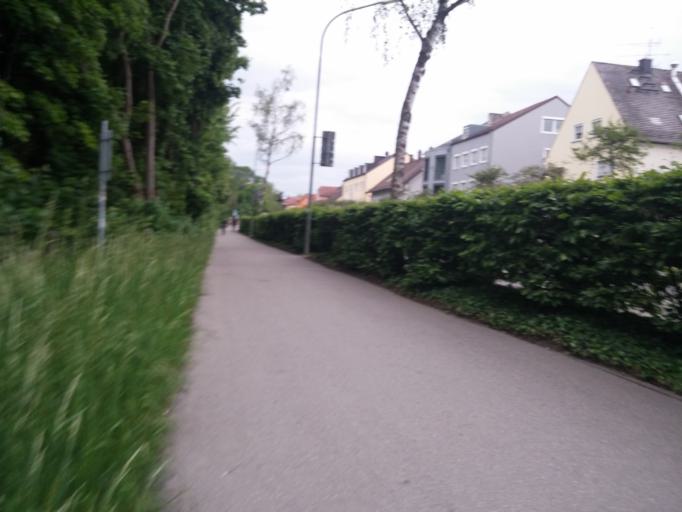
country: DE
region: Bavaria
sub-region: Upper Bavaria
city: Dachau
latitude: 48.2565
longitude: 11.4428
